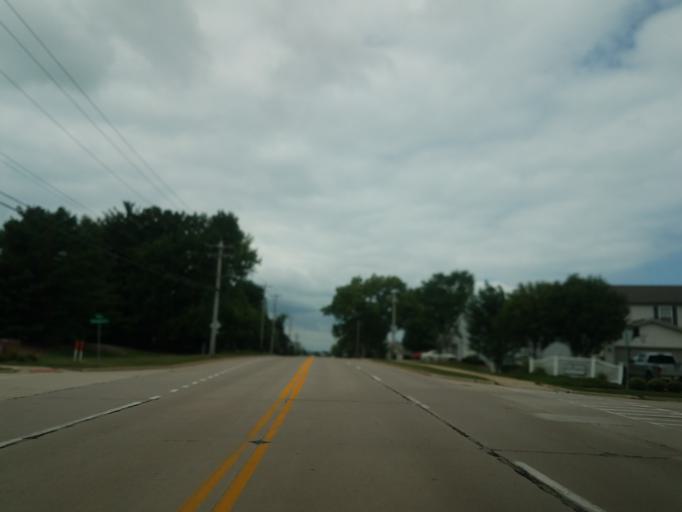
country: US
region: Illinois
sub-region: McLean County
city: Bloomington
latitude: 40.4514
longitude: -89.0305
